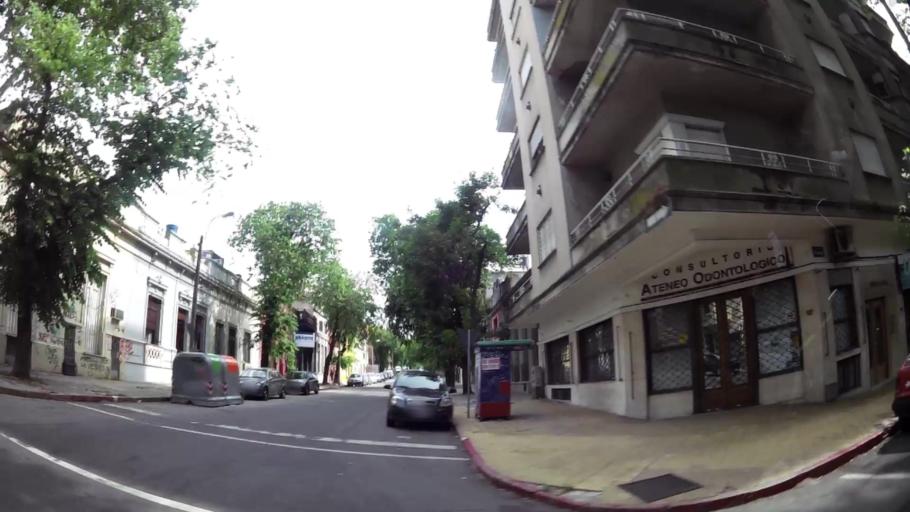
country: UY
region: Montevideo
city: Montevideo
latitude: -34.9070
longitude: -56.1674
